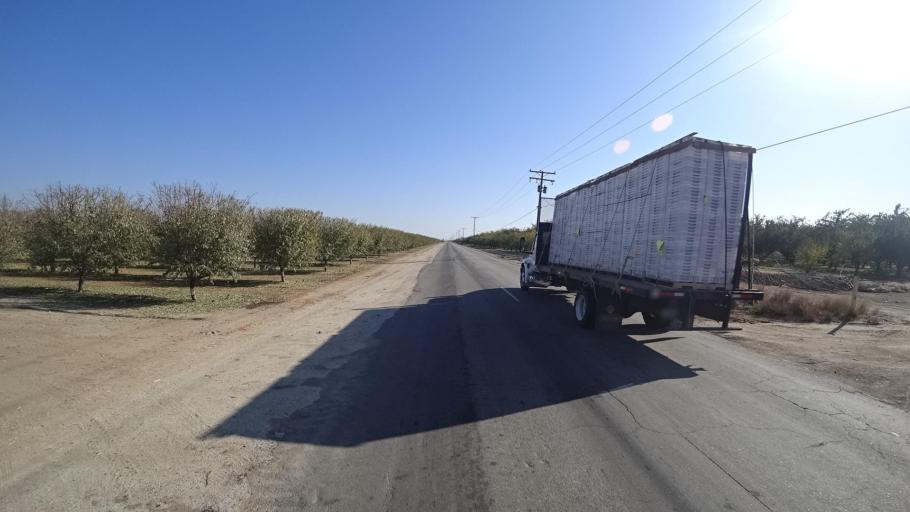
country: US
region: California
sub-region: Kern County
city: McFarland
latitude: 35.7180
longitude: -119.2183
